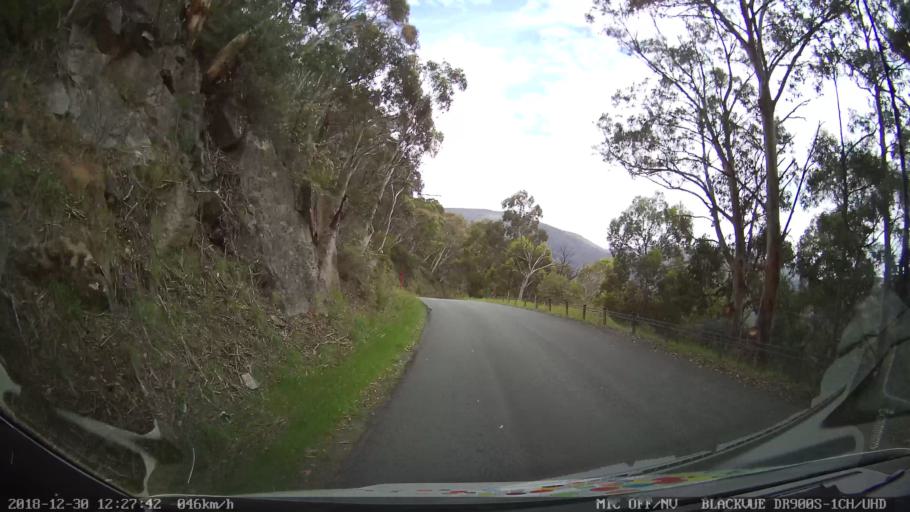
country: AU
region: New South Wales
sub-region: Snowy River
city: Jindabyne
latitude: -36.3292
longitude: 148.4896
